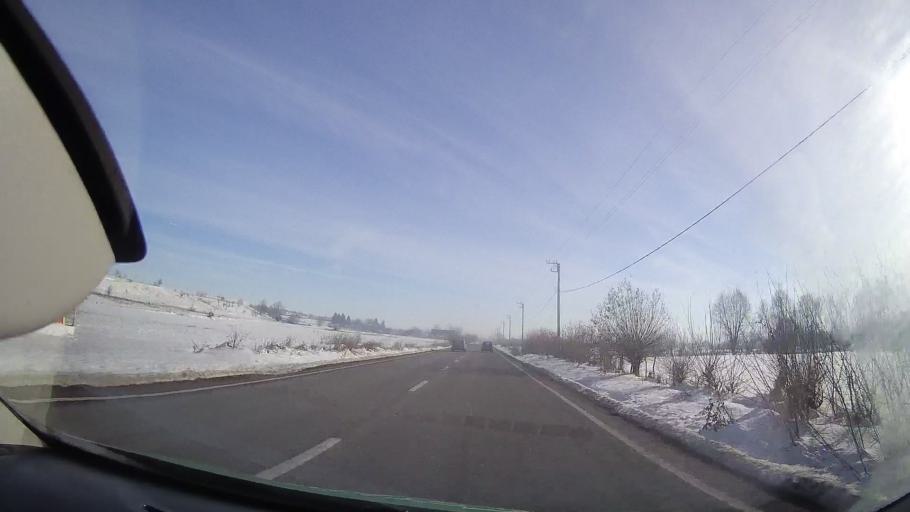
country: RO
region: Neamt
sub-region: Comuna Ghindaoani
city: Ghindaoani
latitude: 47.0824
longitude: 26.3413
